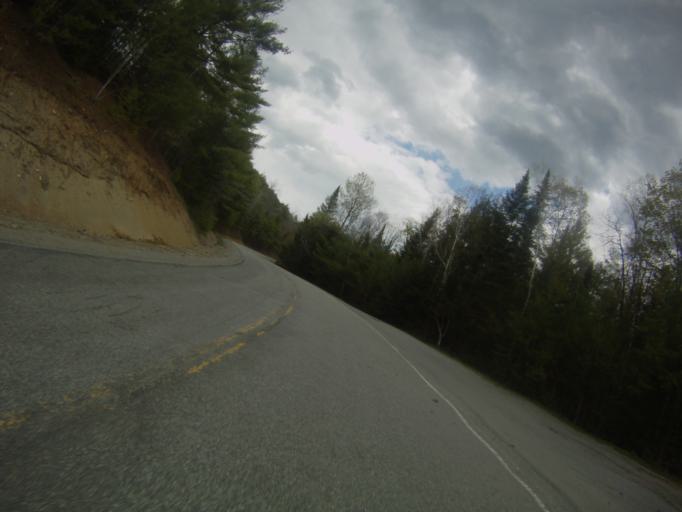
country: US
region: New York
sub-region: Essex County
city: Mineville
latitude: 44.0750
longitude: -73.6387
